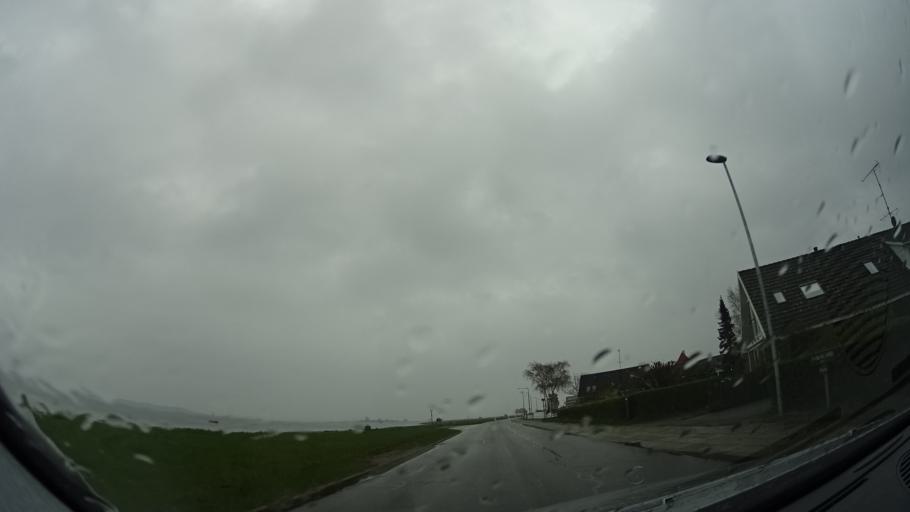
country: DK
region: Zealand
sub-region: Holbaek Kommune
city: Holbaek
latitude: 55.7211
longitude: 11.7428
